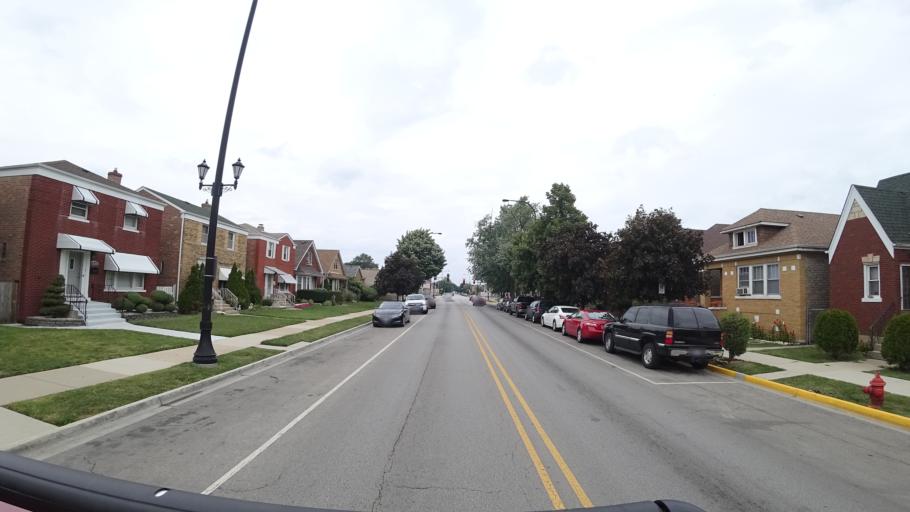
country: US
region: Illinois
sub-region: Cook County
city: Cicero
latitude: 41.8574
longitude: -87.7641
